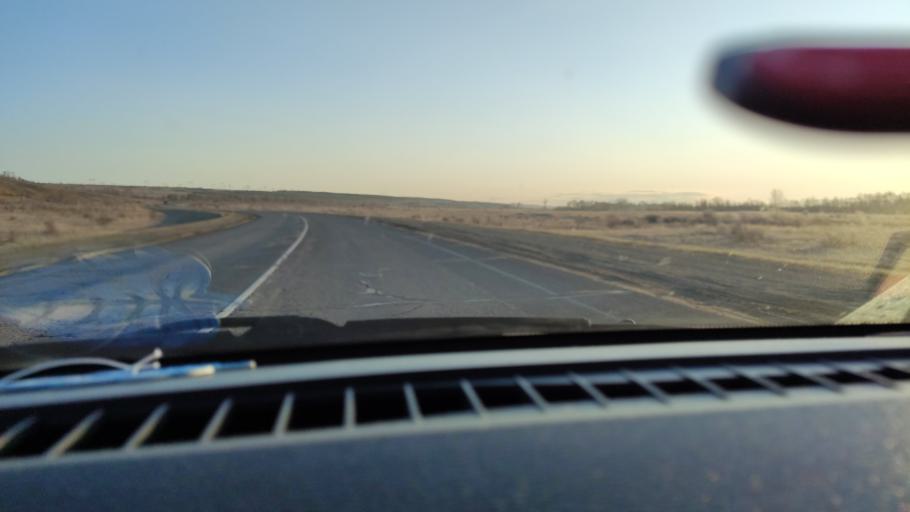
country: RU
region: Saratov
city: Sennoy
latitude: 52.0923
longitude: 46.8111
